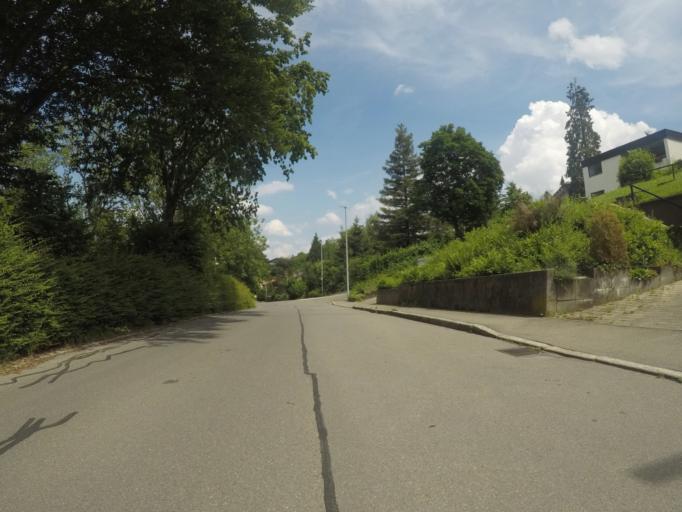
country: DE
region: Baden-Wuerttemberg
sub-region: Tuebingen Region
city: Reutlingen
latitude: 48.4739
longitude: 9.2051
